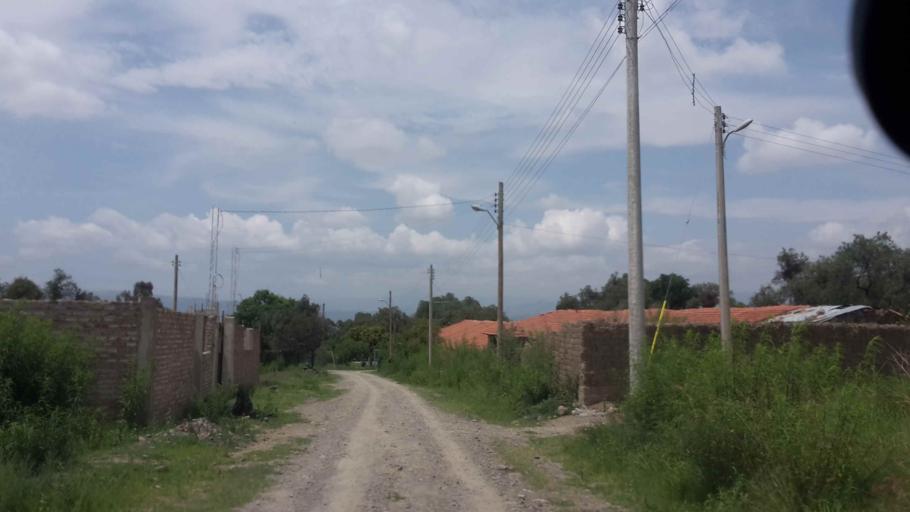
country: BO
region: Cochabamba
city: Cochabamba
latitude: -17.3314
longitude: -66.2140
